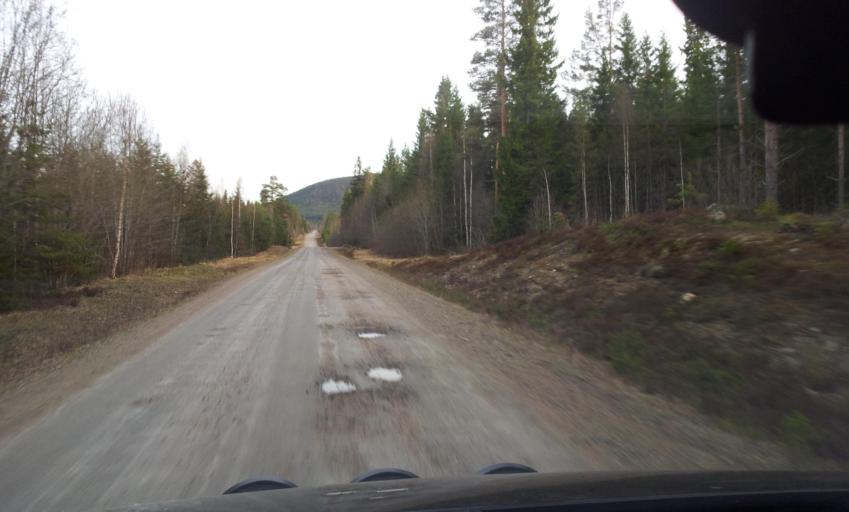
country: SE
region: Gaevleborg
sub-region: Ljusdals Kommun
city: Farila
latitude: 62.0812
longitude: 15.7726
